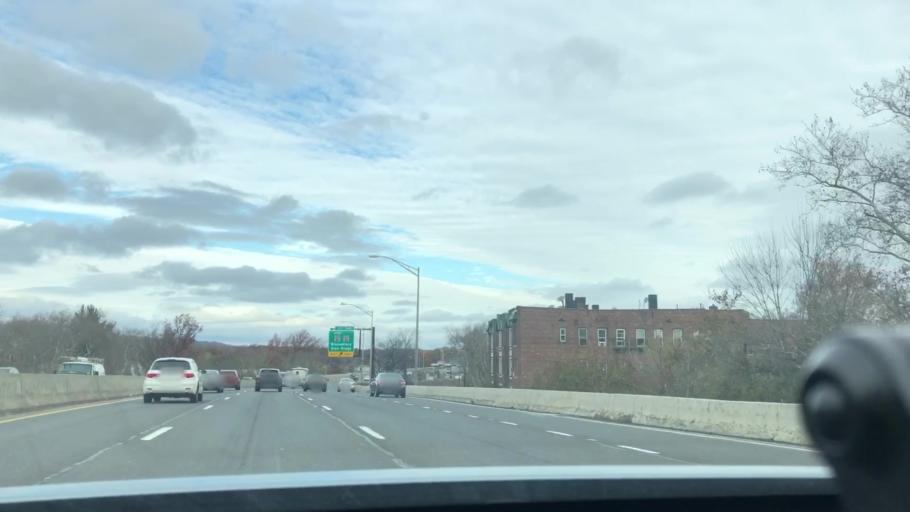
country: US
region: New Jersey
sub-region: Essex County
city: East Orange
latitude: 40.7808
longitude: -74.2011
